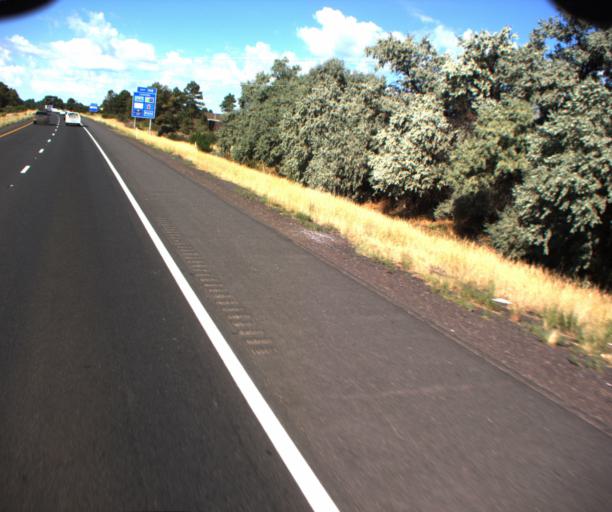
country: US
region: Arizona
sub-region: Coconino County
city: Flagstaff
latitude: 35.2118
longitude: -111.5949
